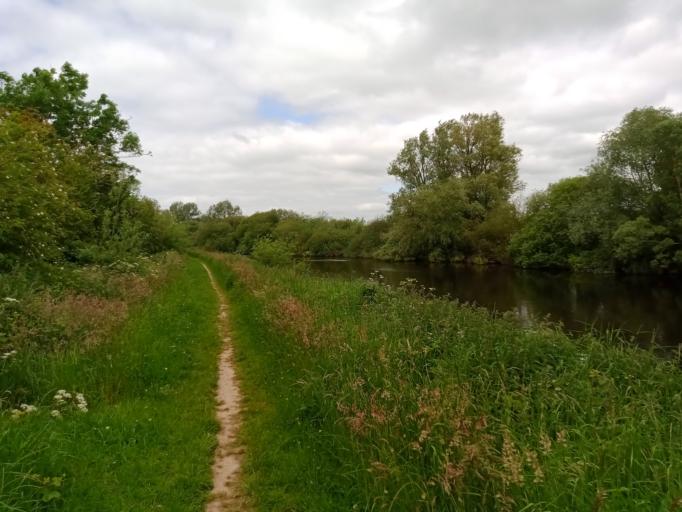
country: IE
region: Leinster
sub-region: County Carlow
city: Carlow
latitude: 52.8030
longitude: -6.9648
